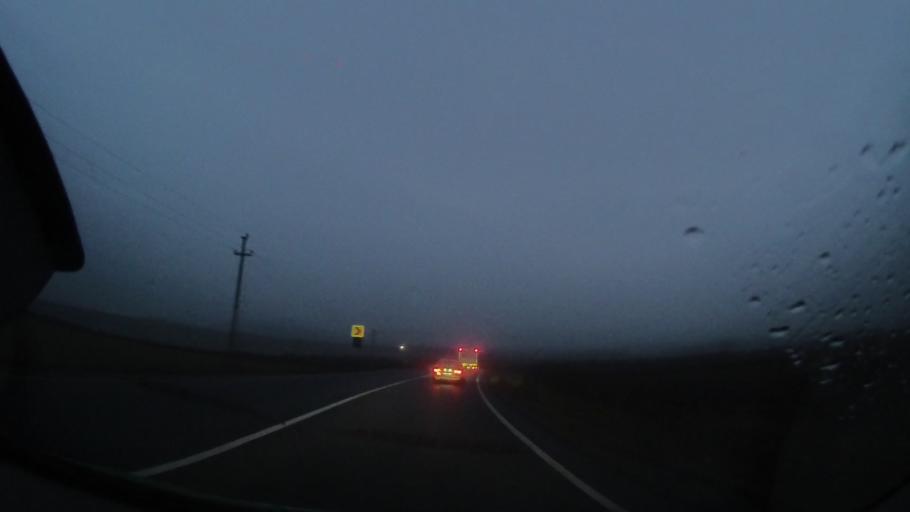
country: RO
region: Harghita
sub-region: Comuna Ditrau
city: Ditrau
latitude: 46.8229
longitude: 25.4921
